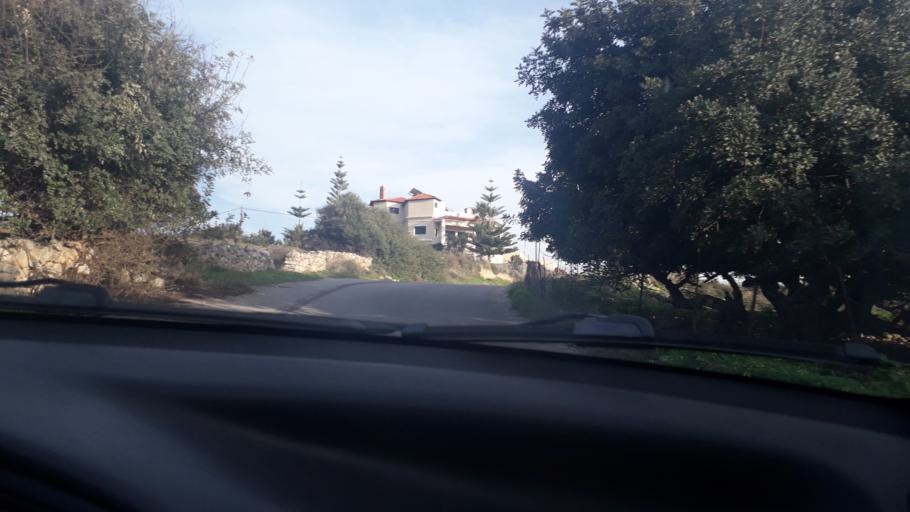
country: GR
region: Crete
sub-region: Nomos Rethymnis
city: Panormos
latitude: 35.3896
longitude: 24.6132
